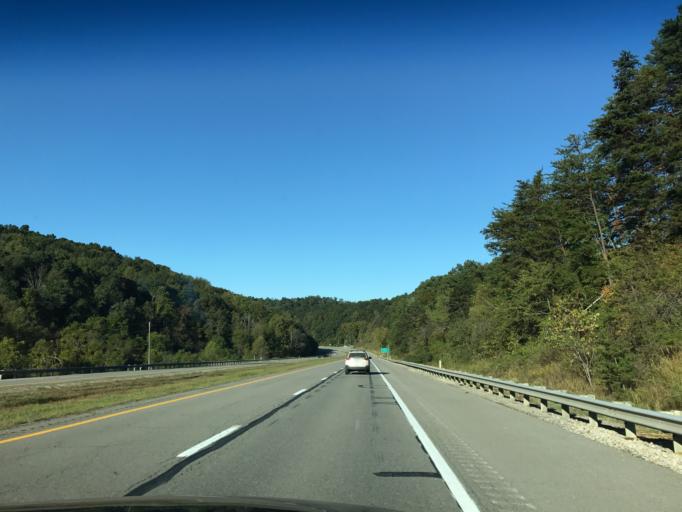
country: US
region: Ohio
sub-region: Washington County
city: Newport
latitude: 39.2591
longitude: -81.2836
